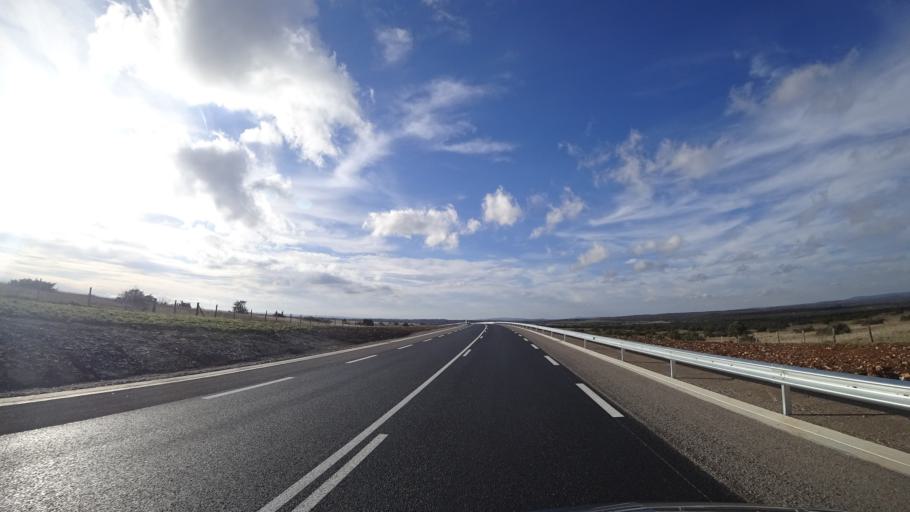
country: FR
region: Midi-Pyrenees
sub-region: Departement de l'Aveyron
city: Sebazac-Concoures
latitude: 44.4164
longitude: 2.6425
